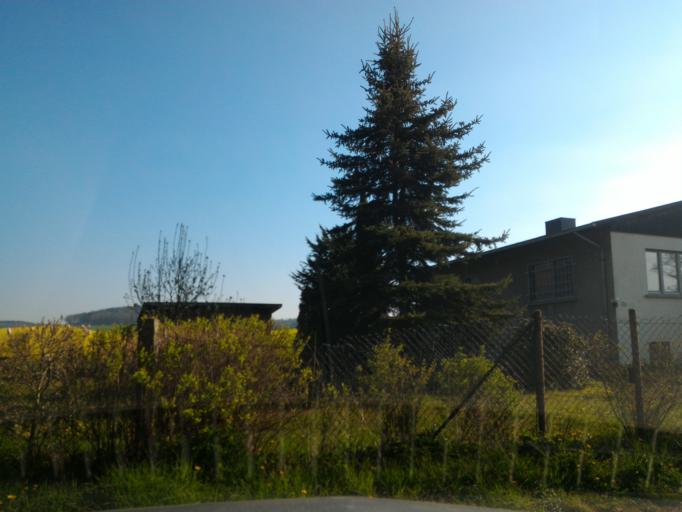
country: DE
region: Saxony
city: Grossschonau
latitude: 50.9051
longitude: 14.6532
